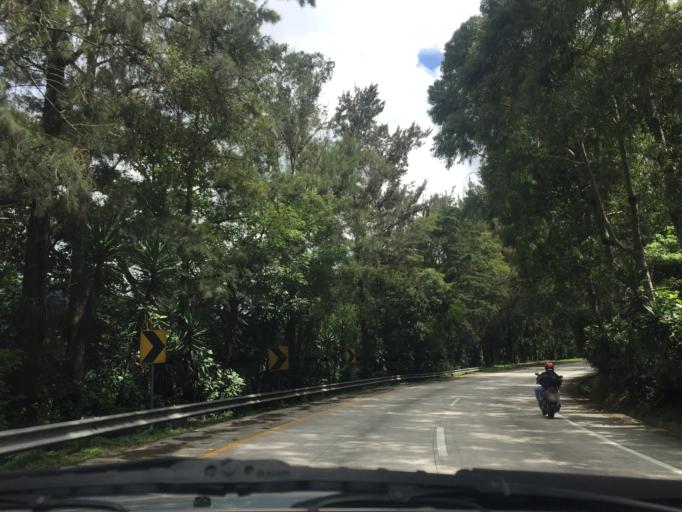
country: GT
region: Sacatepequez
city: Santa Lucia Milpas Altas
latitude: 14.5604
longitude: -90.7023
